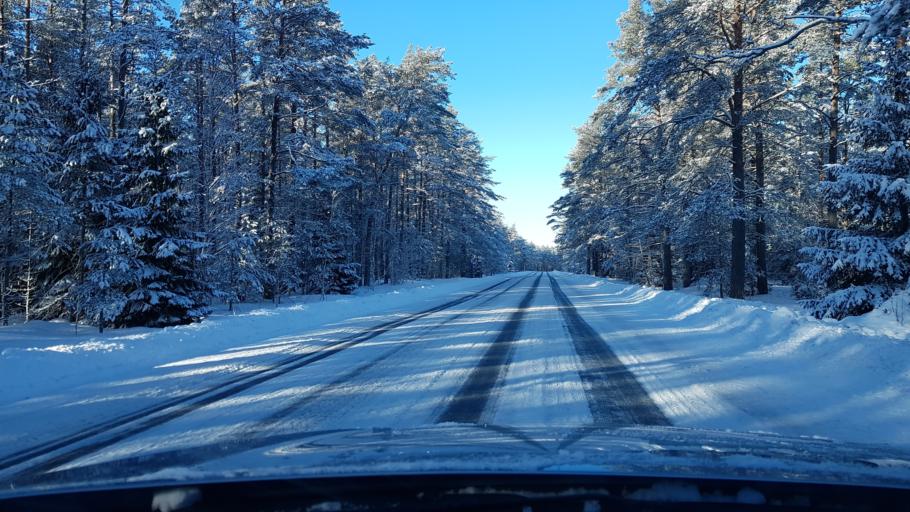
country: EE
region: Hiiumaa
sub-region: Kaerdla linn
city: Kardla
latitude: 58.9243
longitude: 22.7908
